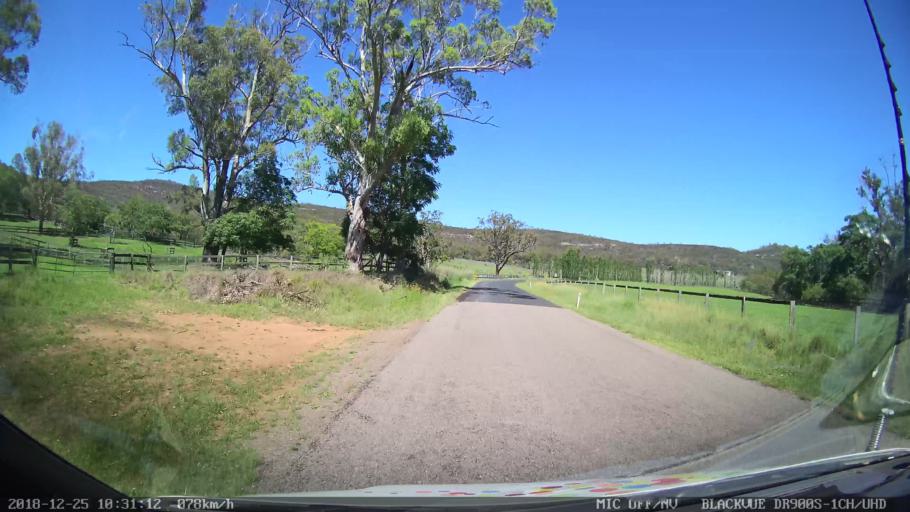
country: AU
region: New South Wales
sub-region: Upper Hunter Shire
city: Merriwa
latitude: -32.3862
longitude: 150.4301
